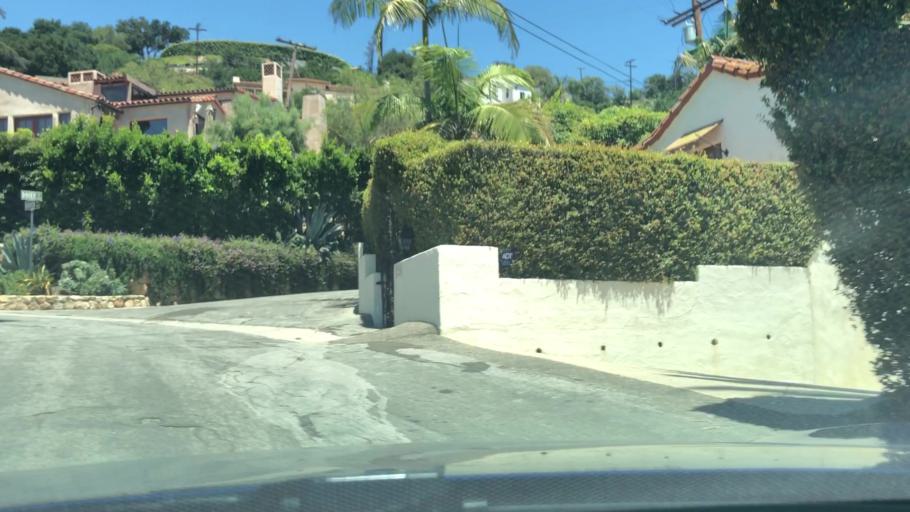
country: US
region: California
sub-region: Santa Barbara County
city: Santa Barbara
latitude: 34.4378
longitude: -119.6934
